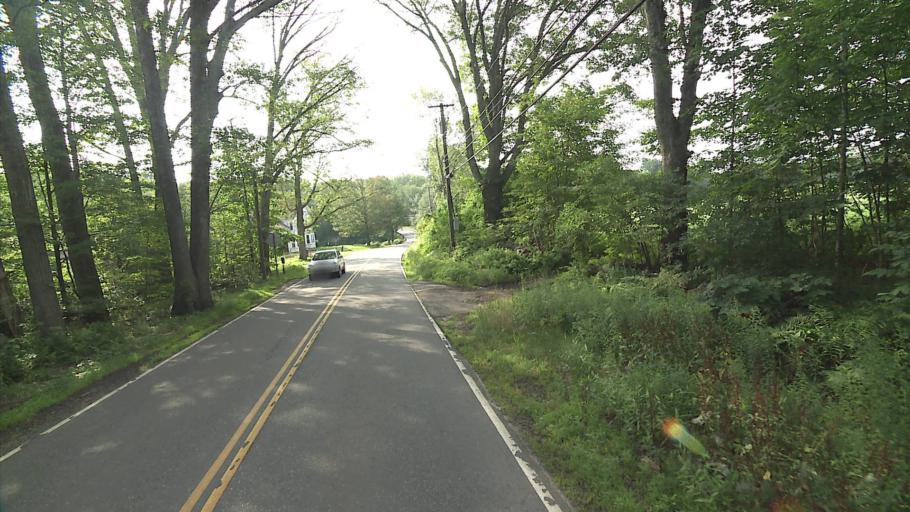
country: US
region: Connecticut
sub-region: Windham County
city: South Woodstock
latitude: 41.9714
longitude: -72.0606
